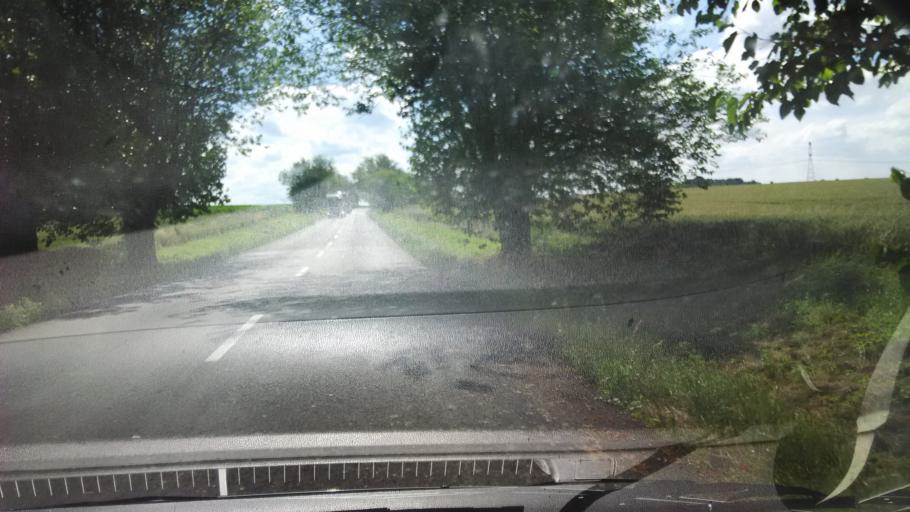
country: SK
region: Nitriansky
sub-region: Okres Nitra
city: Vrable
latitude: 48.1548
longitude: 18.4417
